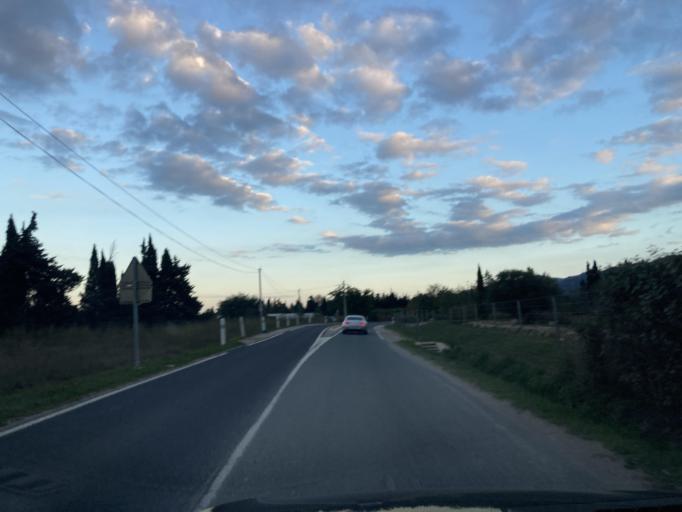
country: FR
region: Languedoc-Roussillon
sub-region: Departement des Pyrenees-Orientales
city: Sant Genis de Fontanes
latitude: 42.5579
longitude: 2.9081
